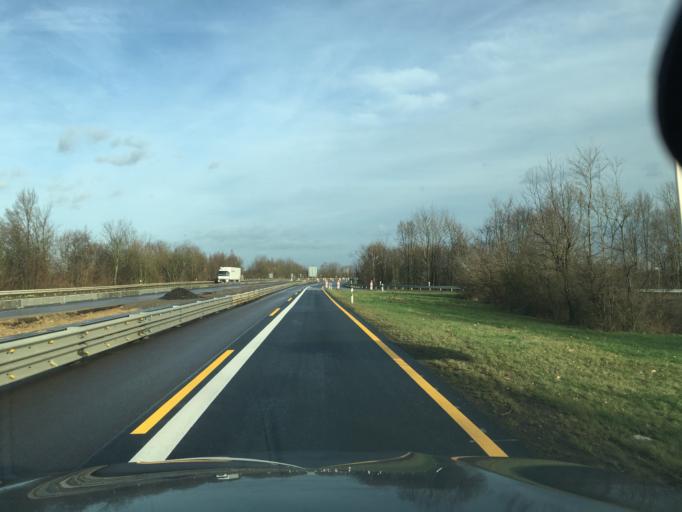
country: DE
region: North Rhine-Westphalia
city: Bruhl
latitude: 50.8044
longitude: 6.9058
